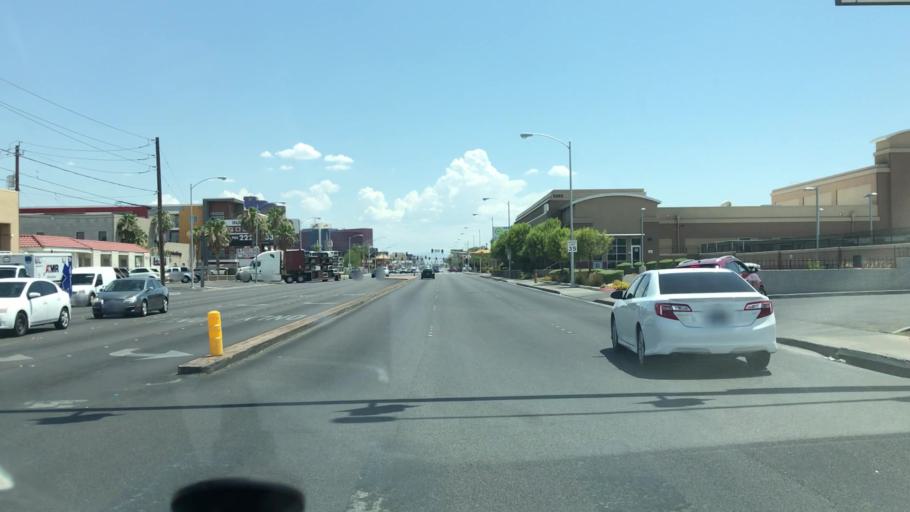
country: US
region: Nevada
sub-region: Clark County
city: Paradise
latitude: 36.1299
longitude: -115.1903
